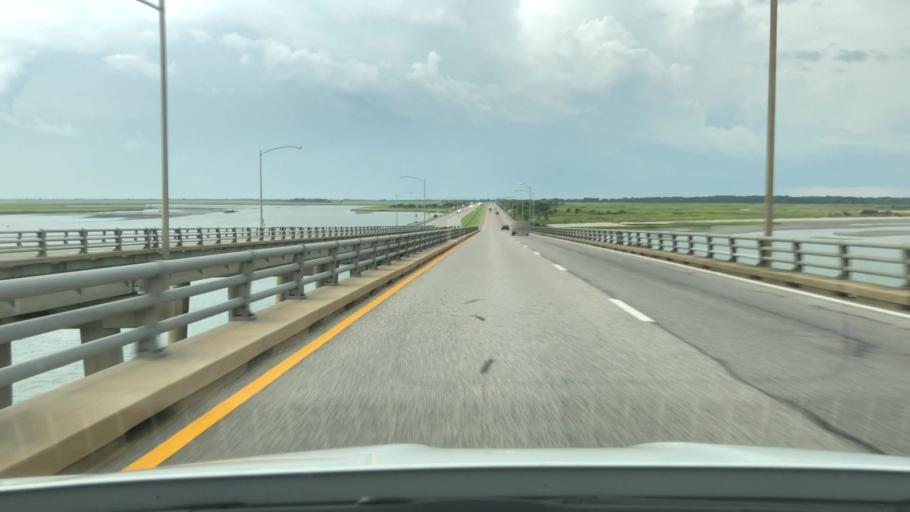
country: US
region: Virginia
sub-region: Northampton County
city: Cape Charles
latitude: 37.1134
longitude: -75.9693
